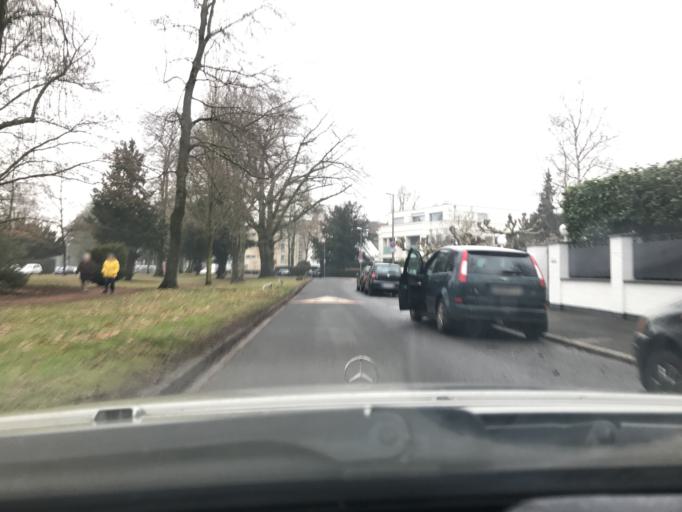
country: DE
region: North Rhine-Westphalia
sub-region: Regierungsbezirk Dusseldorf
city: Krefeld
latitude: 51.3449
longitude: 6.5766
